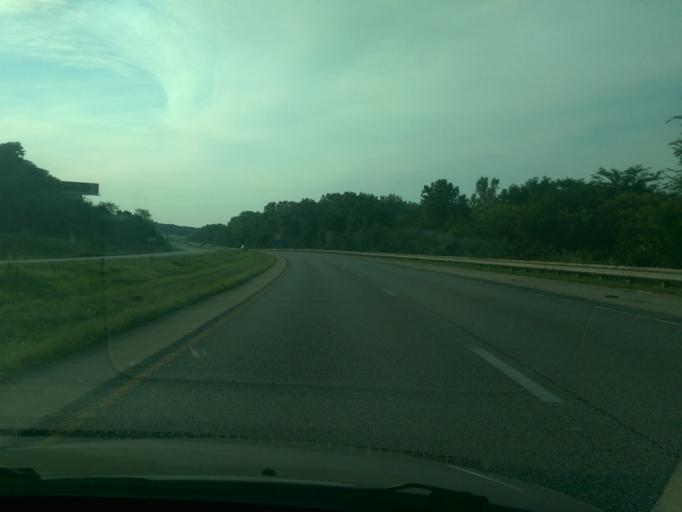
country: US
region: Missouri
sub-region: Platte County
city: Platte City
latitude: 39.3744
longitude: -94.7755
